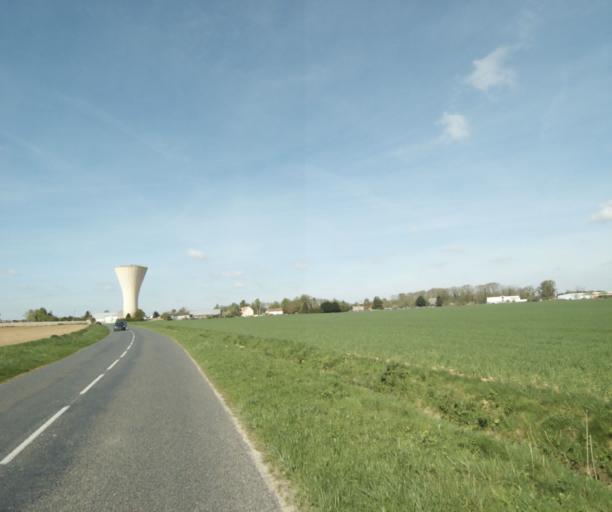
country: FR
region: Ile-de-France
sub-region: Departement de Seine-et-Marne
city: Nangis
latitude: 48.5553
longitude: 3.0306
